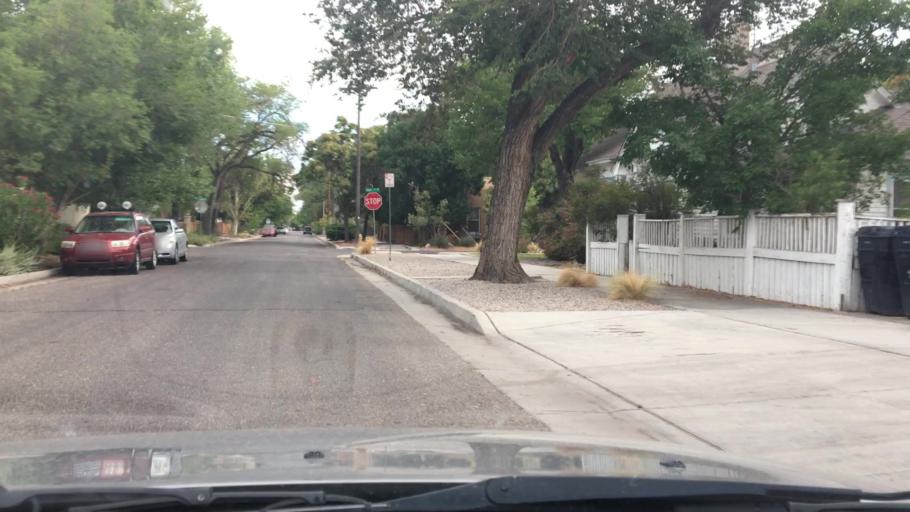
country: US
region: New Mexico
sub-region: Bernalillo County
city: Albuquerque
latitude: 35.0918
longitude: -106.6611
